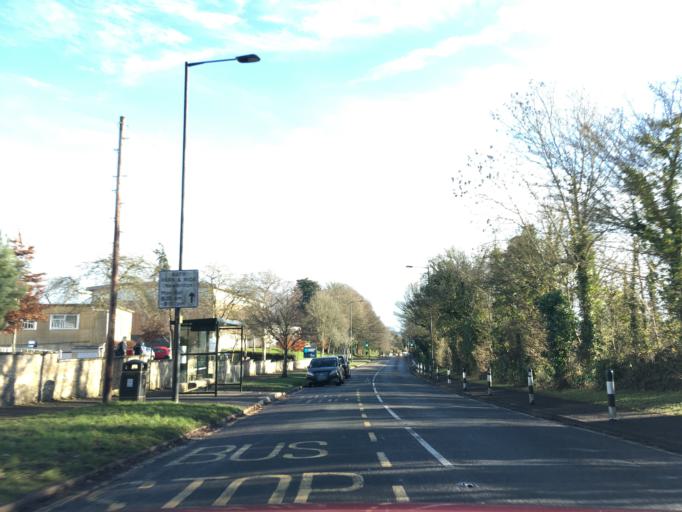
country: GB
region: England
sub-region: Bath and North East Somerset
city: Corston
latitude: 51.3929
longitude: -2.4063
